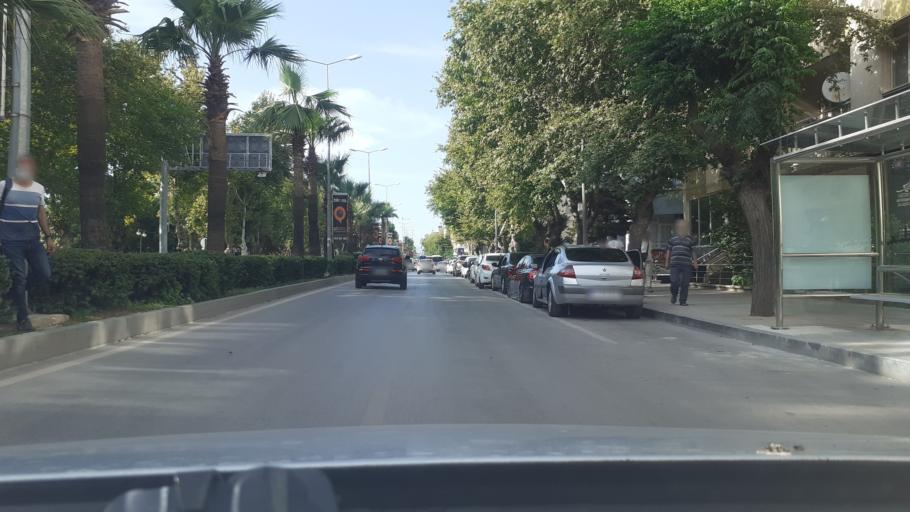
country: TR
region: Hatay
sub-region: Antakya Ilcesi
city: Antakya
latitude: 36.2097
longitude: 36.1594
